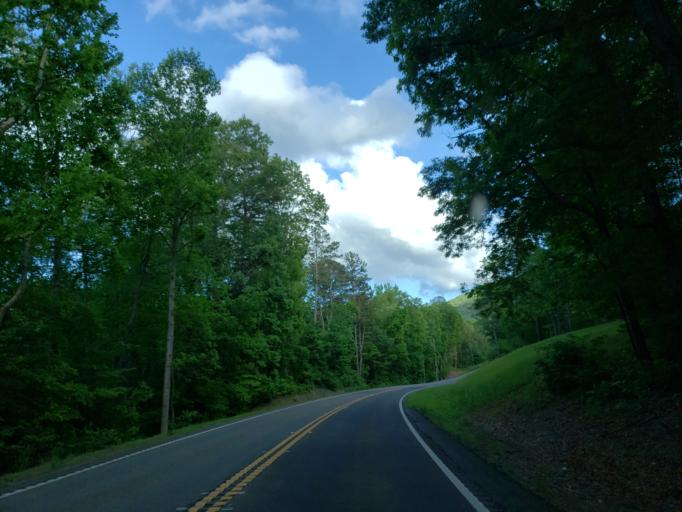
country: US
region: Georgia
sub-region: Bartow County
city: Rydal
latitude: 34.3442
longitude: -84.6375
